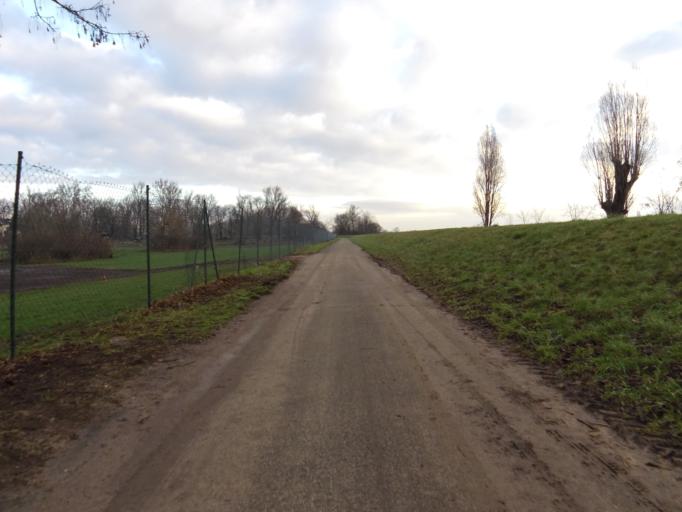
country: DE
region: Hesse
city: Lampertheim
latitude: 49.5710
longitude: 8.4176
